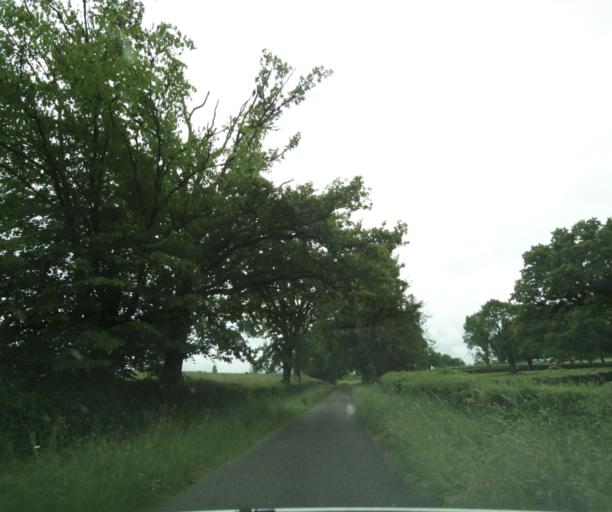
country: FR
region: Bourgogne
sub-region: Departement de Saone-et-Loire
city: Charolles
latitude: 46.4554
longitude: 4.3338
